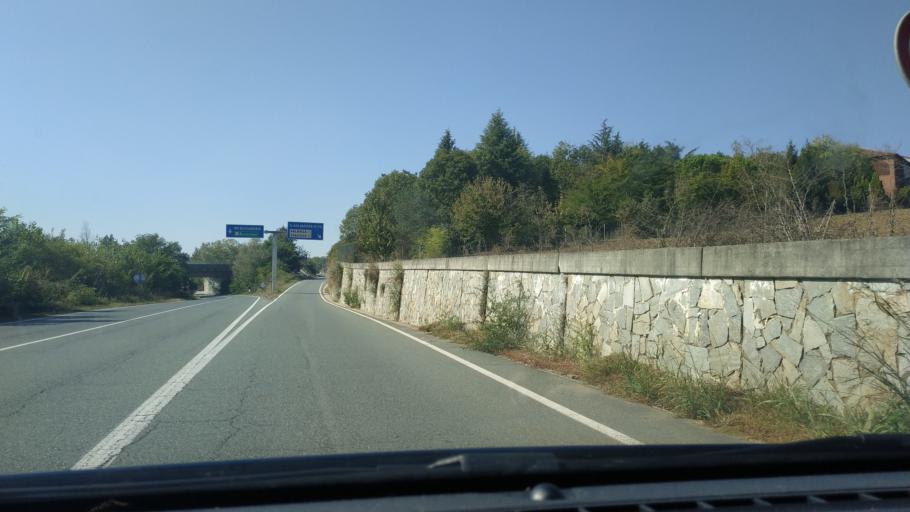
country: IT
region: Piedmont
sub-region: Provincia di Alessandria
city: Valenza
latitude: 45.0267
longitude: 8.6303
